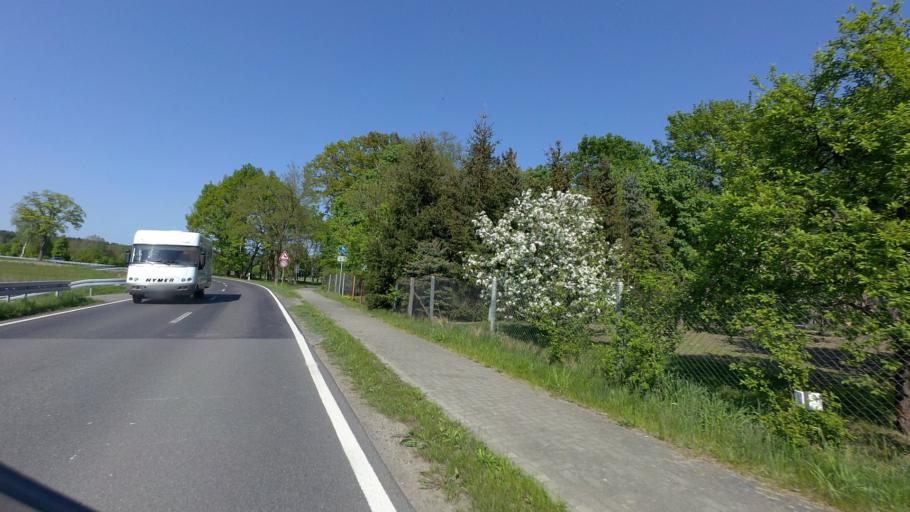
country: DE
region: Brandenburg
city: Neu Zauche
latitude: 52.0208
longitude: 14.0417
